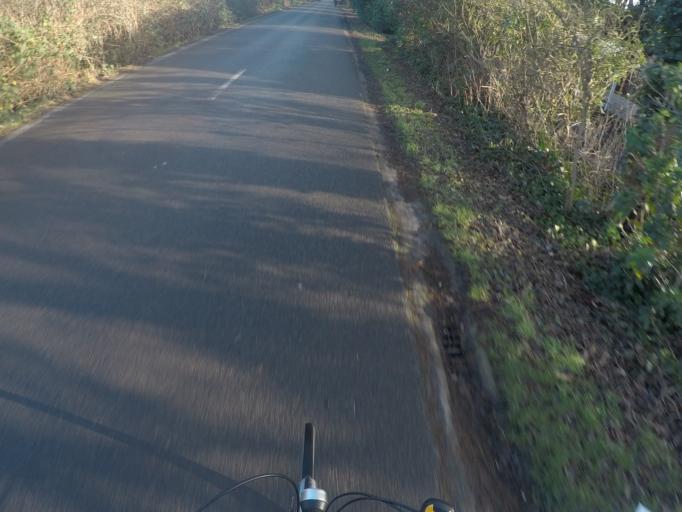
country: BE
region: Flanders
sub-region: Provincie Antwerpen
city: Brasschaat
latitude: 51.3181
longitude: 4.5587
